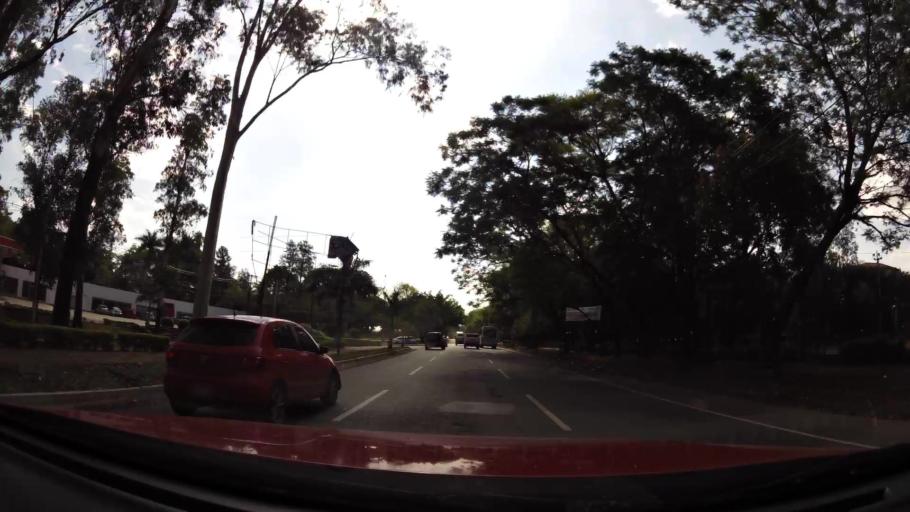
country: PY
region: Central
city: Fernando de la Mora
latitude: -25.3401
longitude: -57.5201
